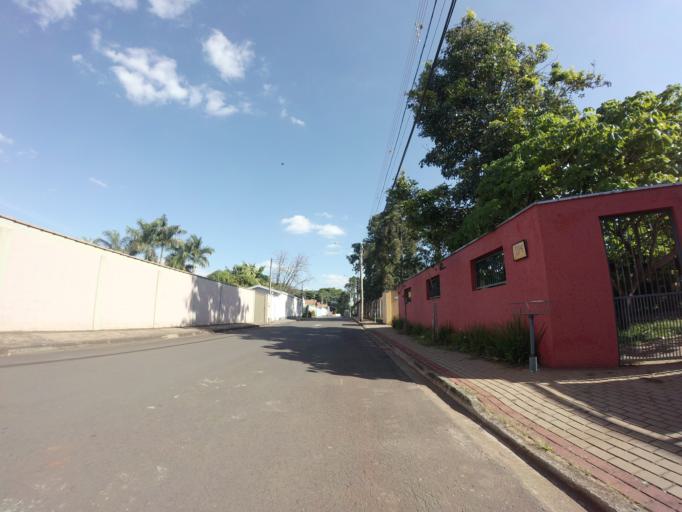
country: BR
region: Sao Paulo
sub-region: Piracicaba
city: Piracicaba
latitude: -22.7404
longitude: -47.5936
